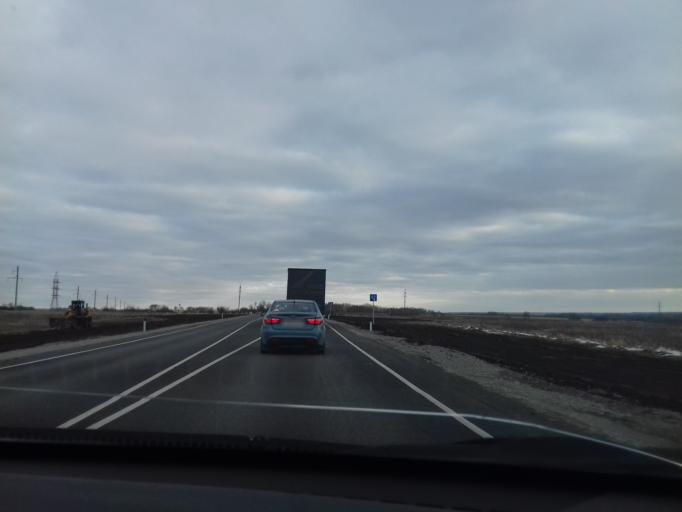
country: RU
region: Kurgan
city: Kataysk
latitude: 56.2941
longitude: 62.6704
